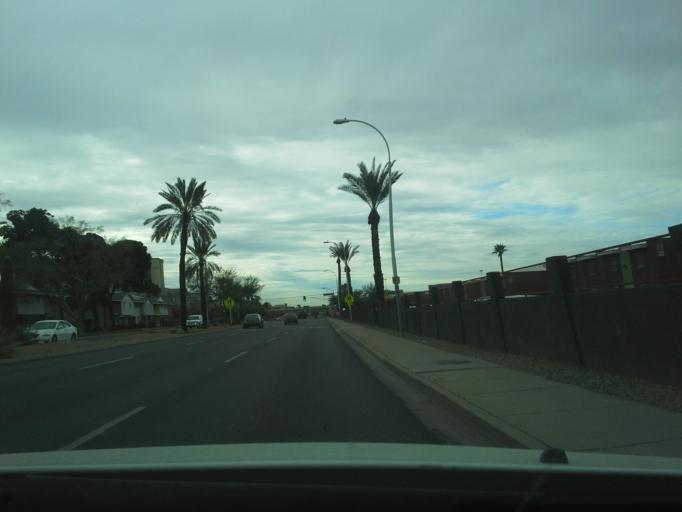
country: US
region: Arizona
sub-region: Maricopa County
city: Tempe Junction
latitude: 33.4637
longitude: -111.9872
